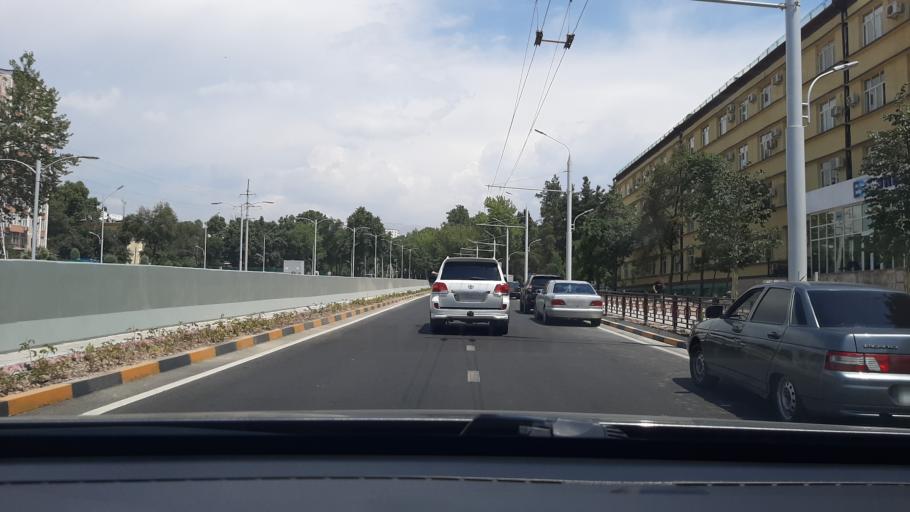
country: TJ
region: Dushanbe
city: Dushanbe
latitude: 38.5855
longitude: 68.7555
